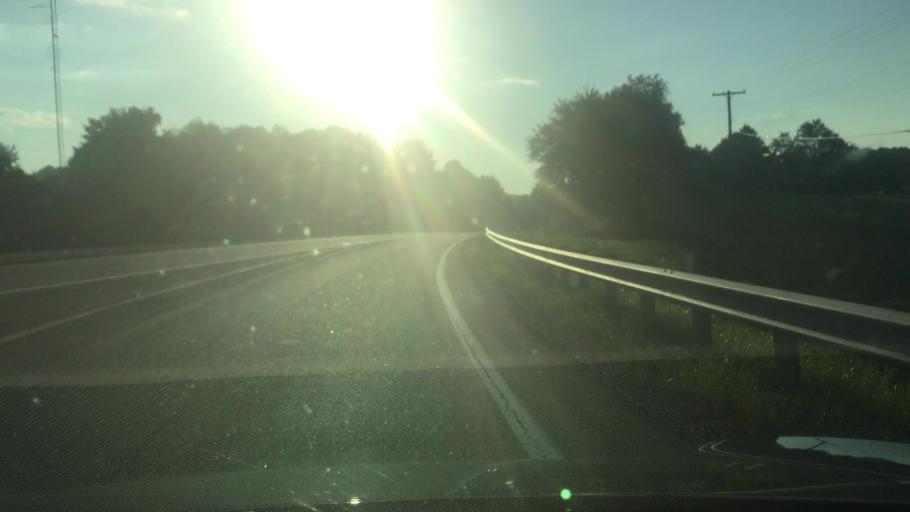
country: US
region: Virginia
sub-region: City of Bedford
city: Bedford
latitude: 37.3250
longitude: -79.5343
